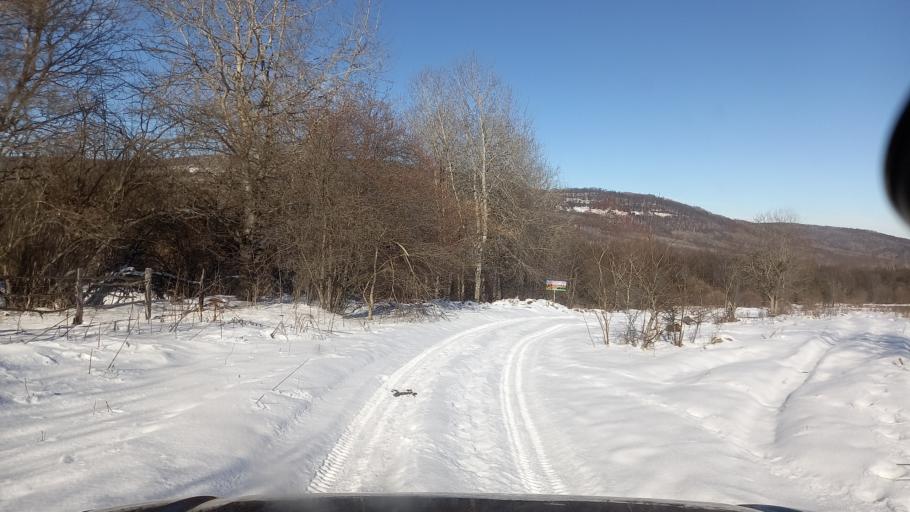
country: RU
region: Adygeya
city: Kamennomostskiy
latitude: 44.2365
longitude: 40.1501
